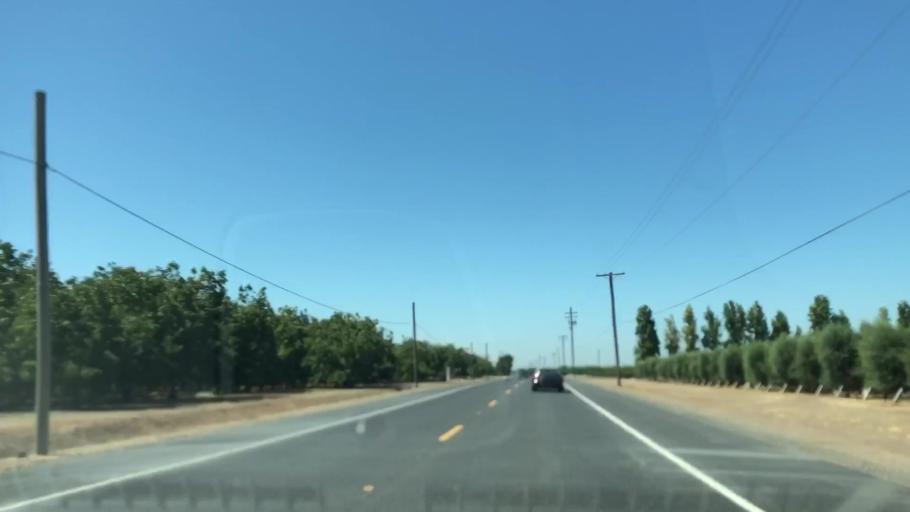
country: US
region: California
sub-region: San Joaquin County
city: Linden
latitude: 37.9331
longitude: -121.0525
